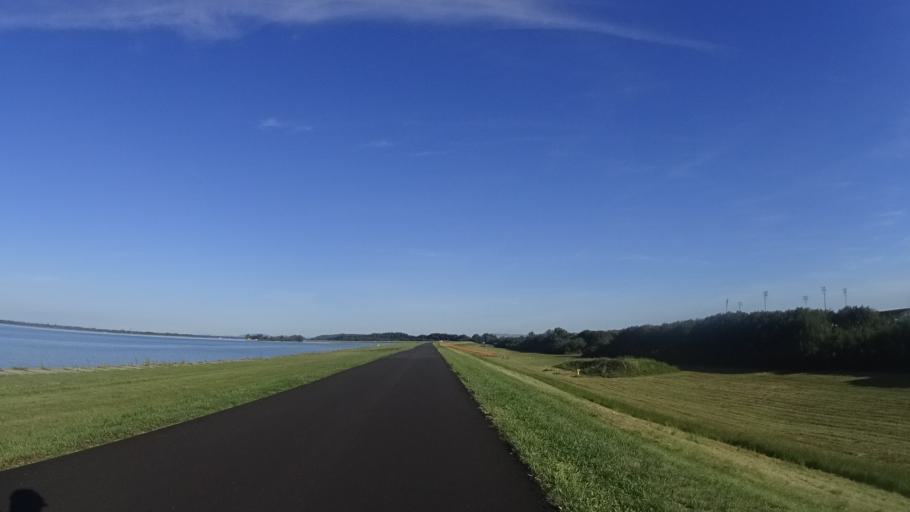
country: SK
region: Trnavsky
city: Samorin
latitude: 48.0135
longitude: 17.2980
